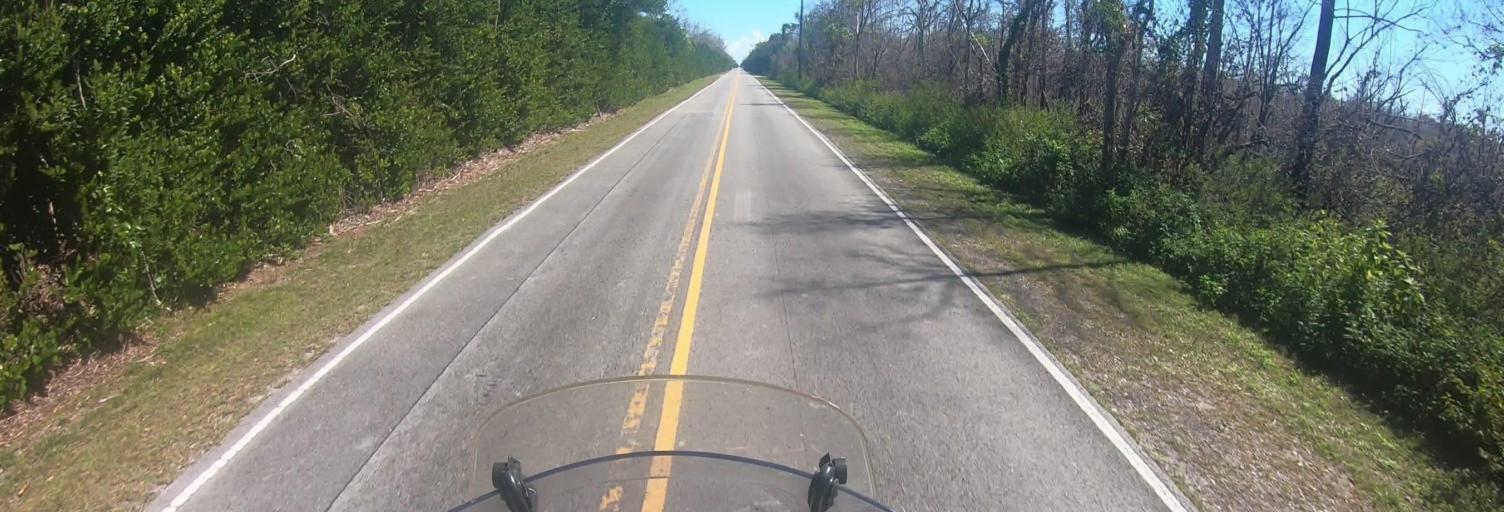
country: US
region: Florida
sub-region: Miami-Dade County
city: Kendall West
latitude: 25.7607
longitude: -80.8637
